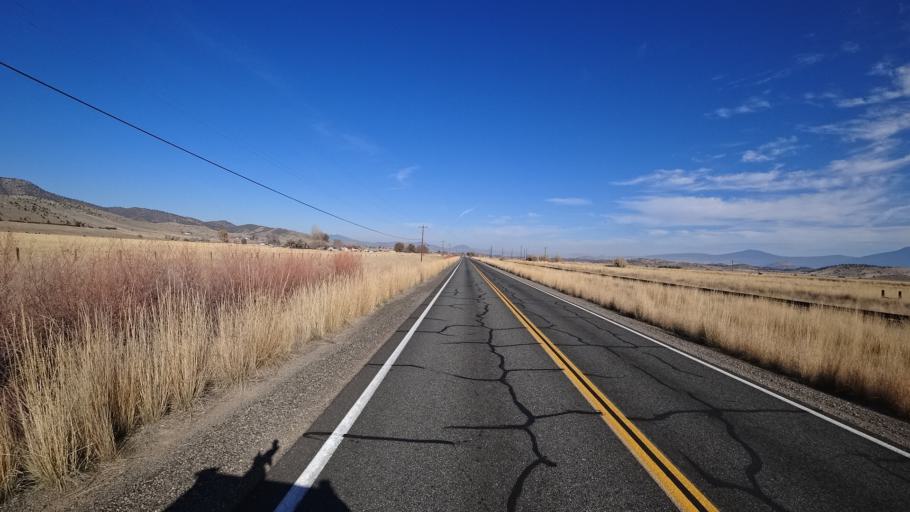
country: US
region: California
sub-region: Siskiyou County
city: Montague
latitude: 41.5985
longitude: -122.5237
